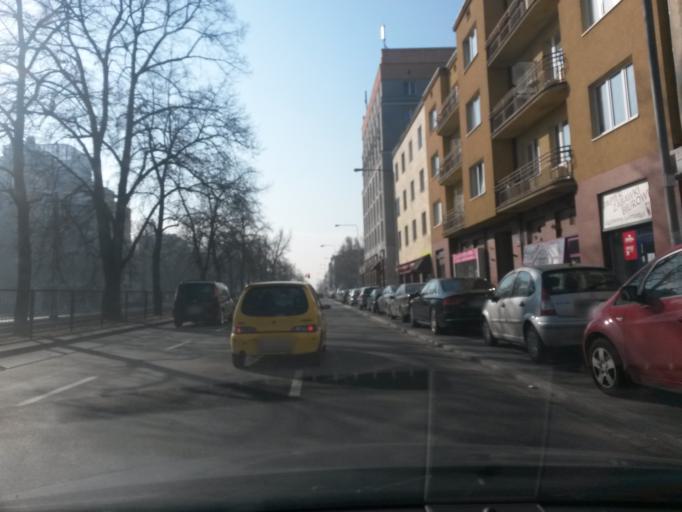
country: PL
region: Masovian Voivodeship
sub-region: Warszawa
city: Mokotow
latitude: 52.1962
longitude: 21.0240
